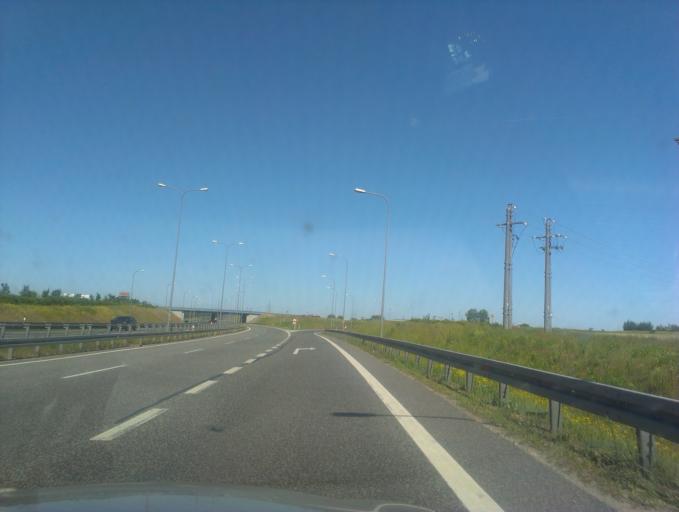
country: PL
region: Pomeranian Voivodeship
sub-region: Powiat chojnicki
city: Chojnice
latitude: 53.6873
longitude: 17.6147
